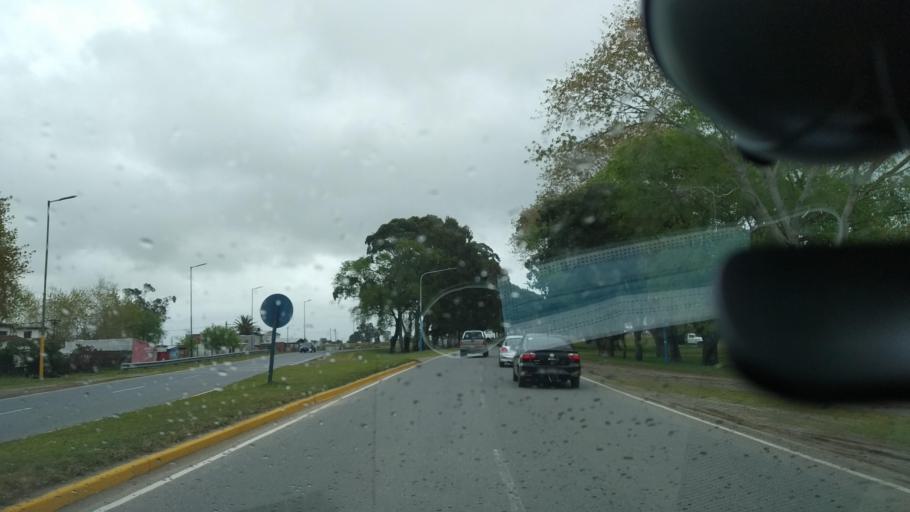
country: AR
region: Buenos Aires
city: San Clemente del Tuyu
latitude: -36.3862
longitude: -56.7284
